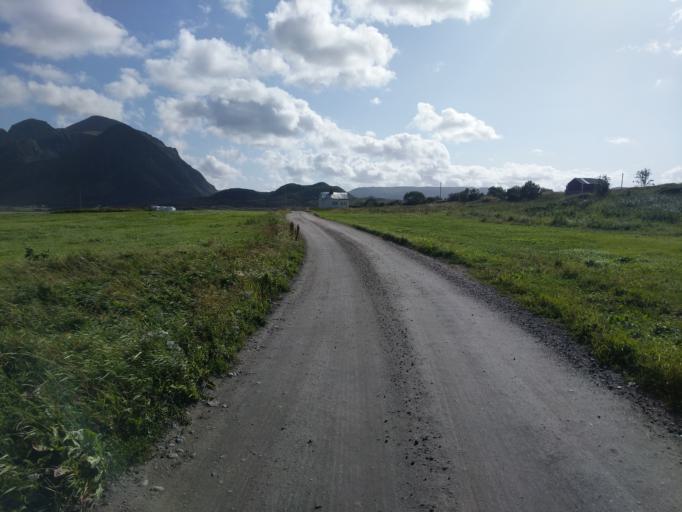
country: NO
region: Nordland
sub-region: Vestvagoy
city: Evjen
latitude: 68.3364
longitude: 13.8864
